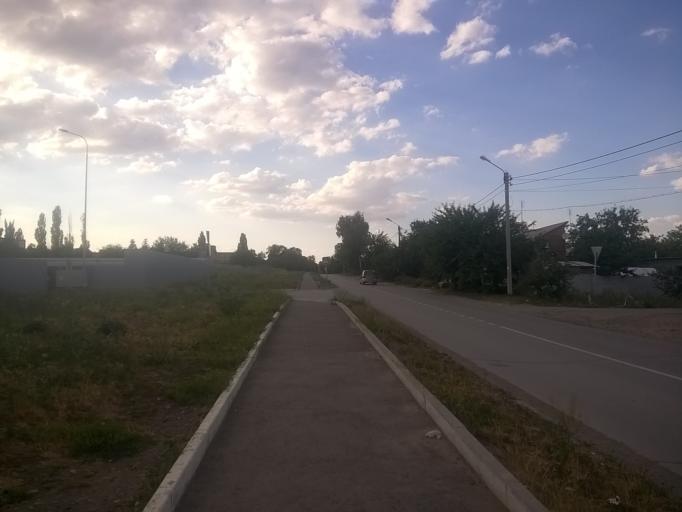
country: RU
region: Rostov
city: Donetsk
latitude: 48.3314
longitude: 39.9532
